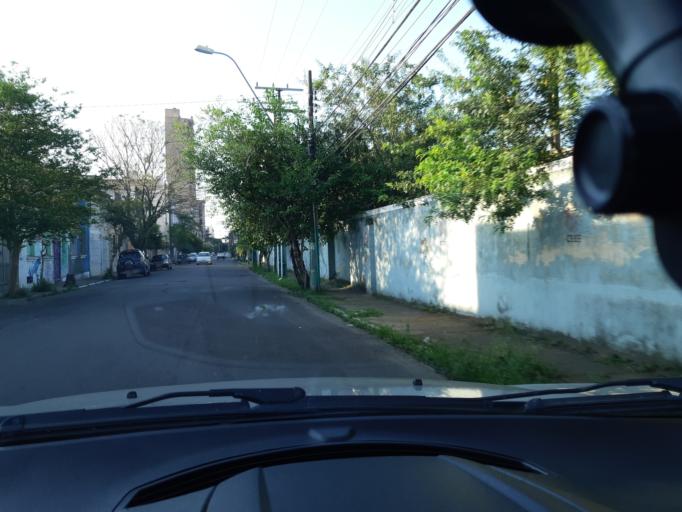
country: BR
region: Rio Grande do Sul
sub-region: Sao Leopoldo
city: Sao Leopoldo
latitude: -29.7663
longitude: -51.1415
